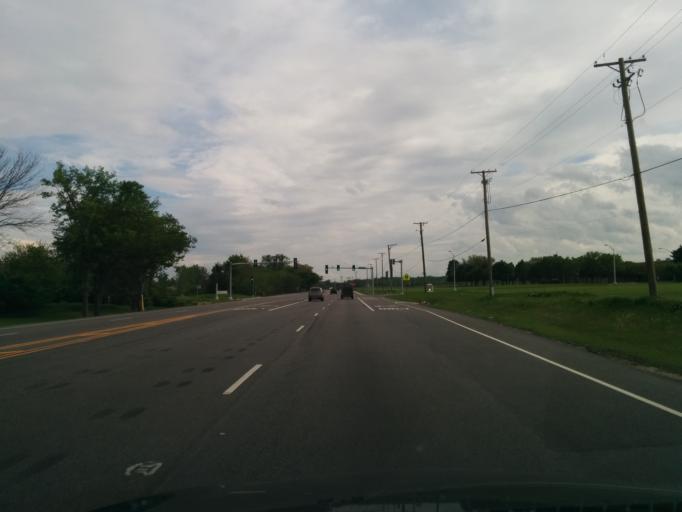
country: US
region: Illinois
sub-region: Will County
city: Romeoville
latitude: 41.6302
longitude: -88.0805
